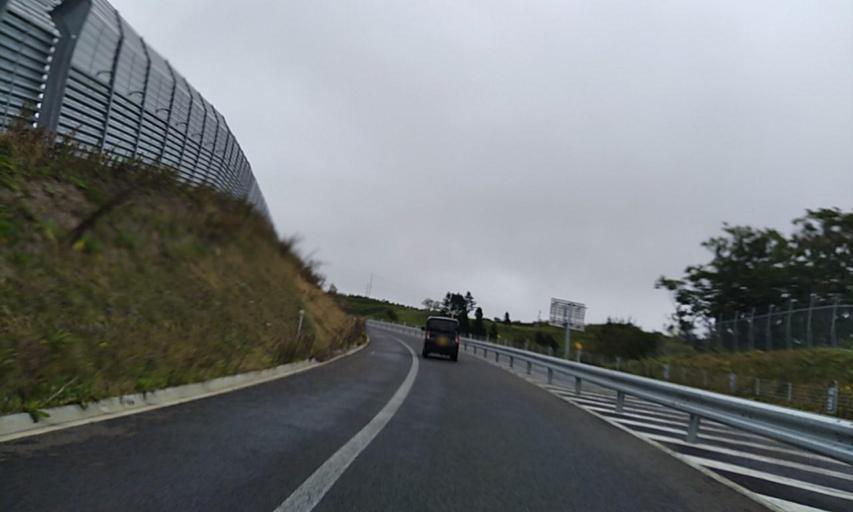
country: JP
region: Hokkaido
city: Nemuro
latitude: 43.2750
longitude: 145.5053
